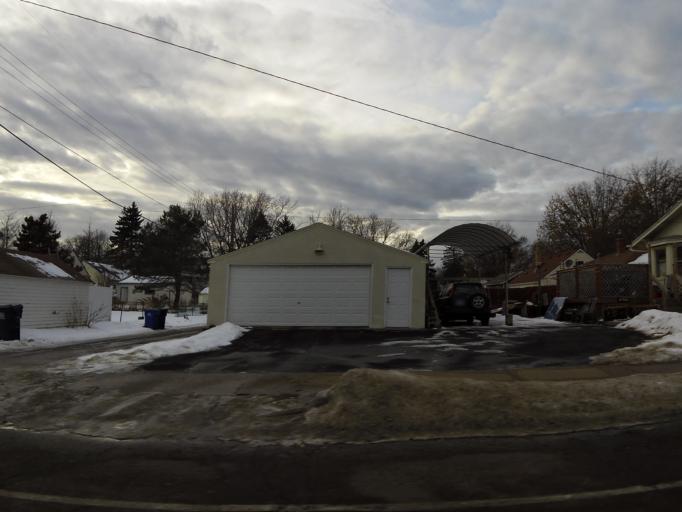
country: US
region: Minnesota
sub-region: Ramsey County
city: Maplewood
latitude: 44.9583
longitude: -93.0153
